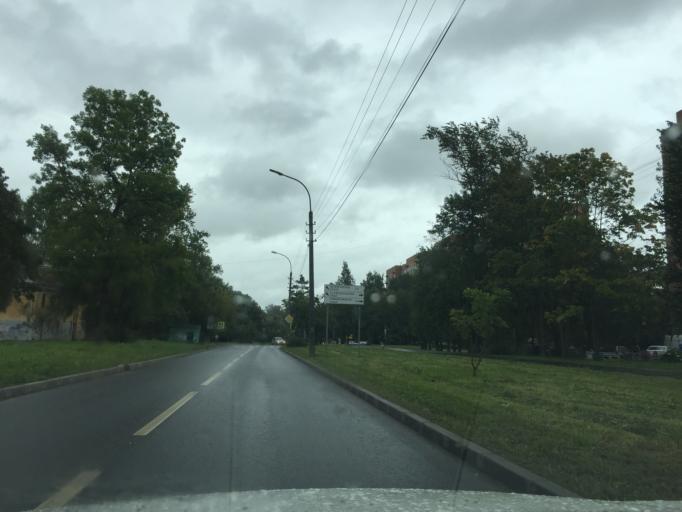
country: RU
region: St.-Petersburg
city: Sosnovaya Polyana
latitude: 59.8452
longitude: 30.1421
